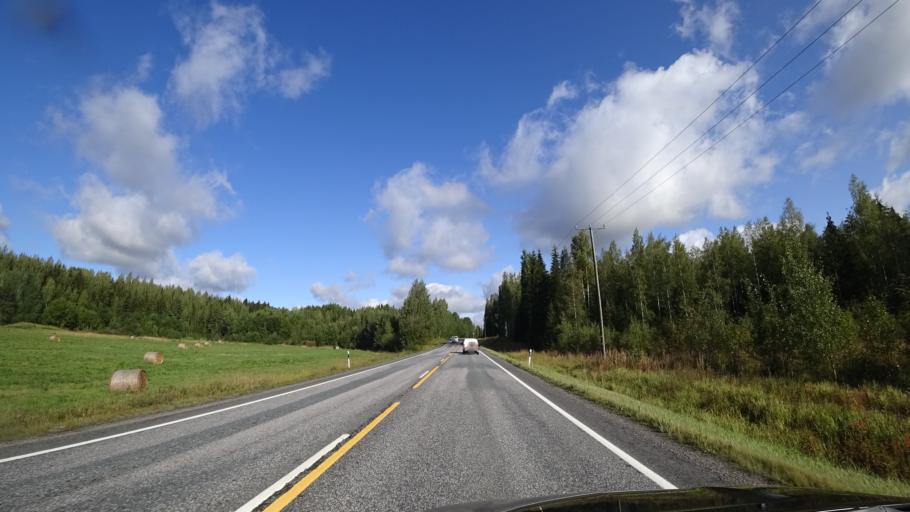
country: FI
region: Uusimaa
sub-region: Helsinki
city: Tuusula
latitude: 60.4748
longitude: 24.9415
